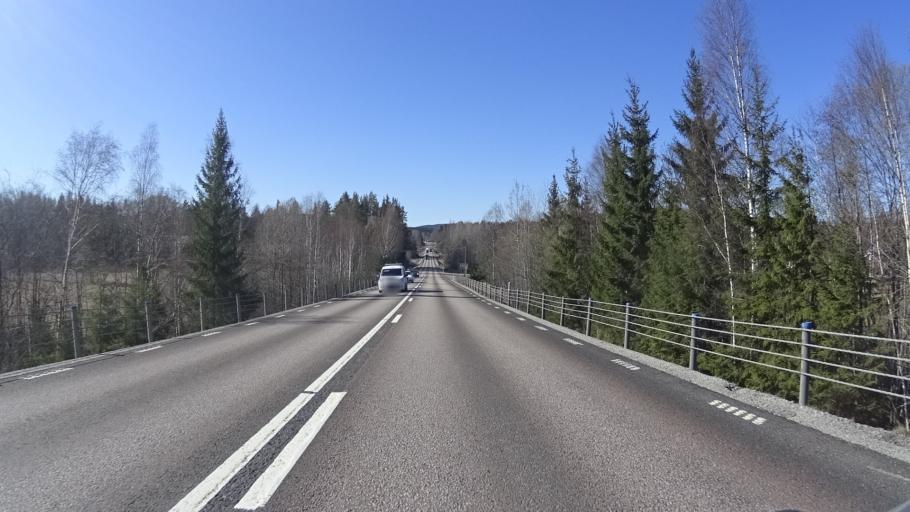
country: SE
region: Vaermland
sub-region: Sunne Kommun
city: Sunne
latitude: 59.6601
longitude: 12.9313
